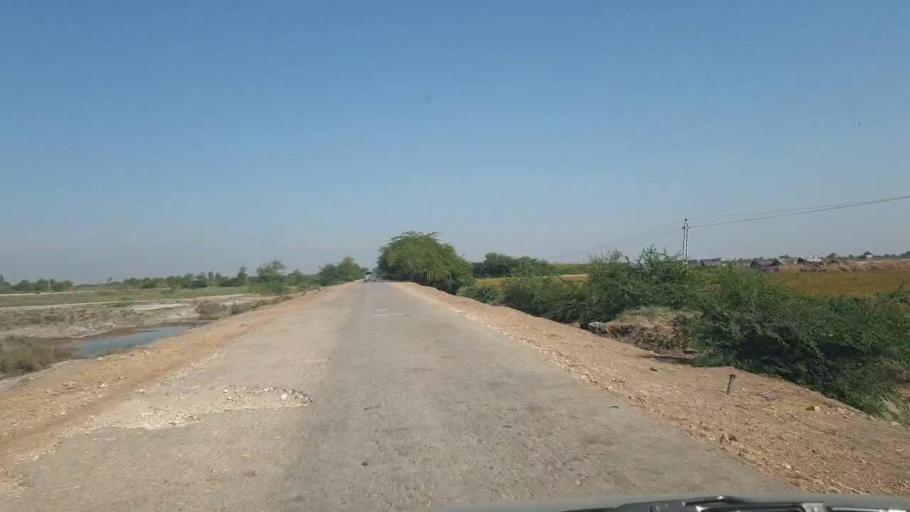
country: PK
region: Sindh
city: Tando Bago
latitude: 24.8102
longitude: 68.9812
